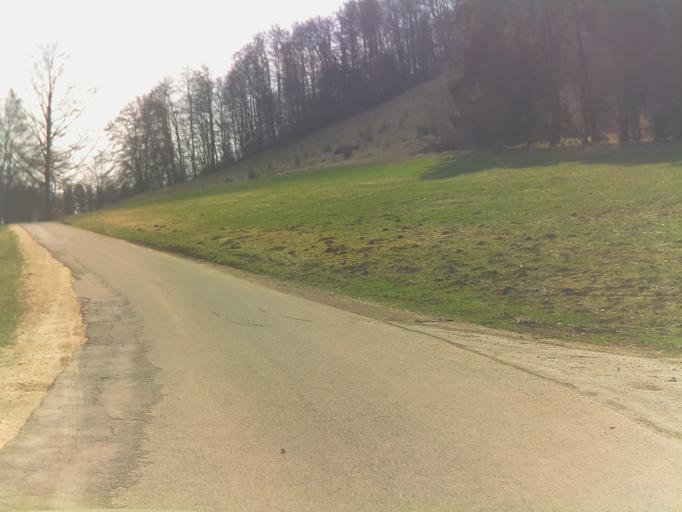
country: DE
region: Baden-Wuerttemberg
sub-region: Tuebingen Region
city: Gomadingen
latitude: 48.4331
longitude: 9.4296
